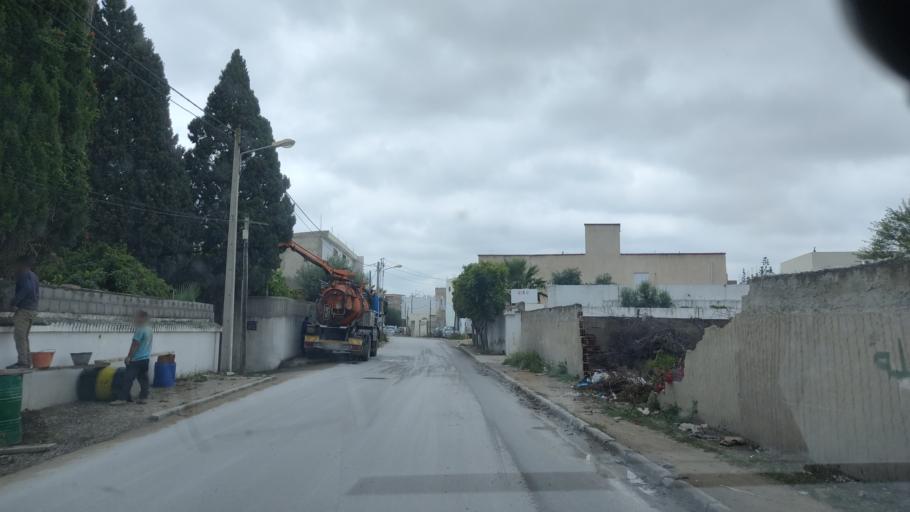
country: TN
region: Ariana
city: Ariana
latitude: 36.8793
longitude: 10.2181
